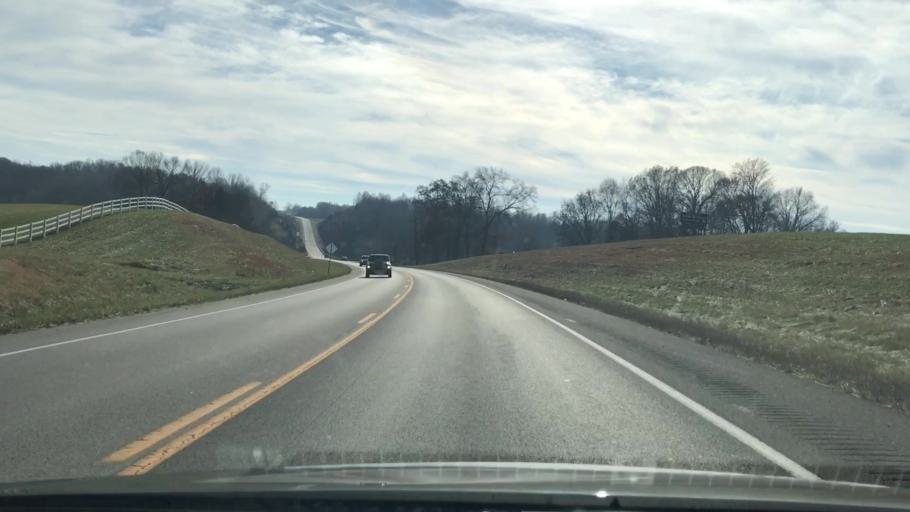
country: US
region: Kentucky
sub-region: Monroe County
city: Tompkinsville
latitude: 36.7517
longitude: -85.6913
